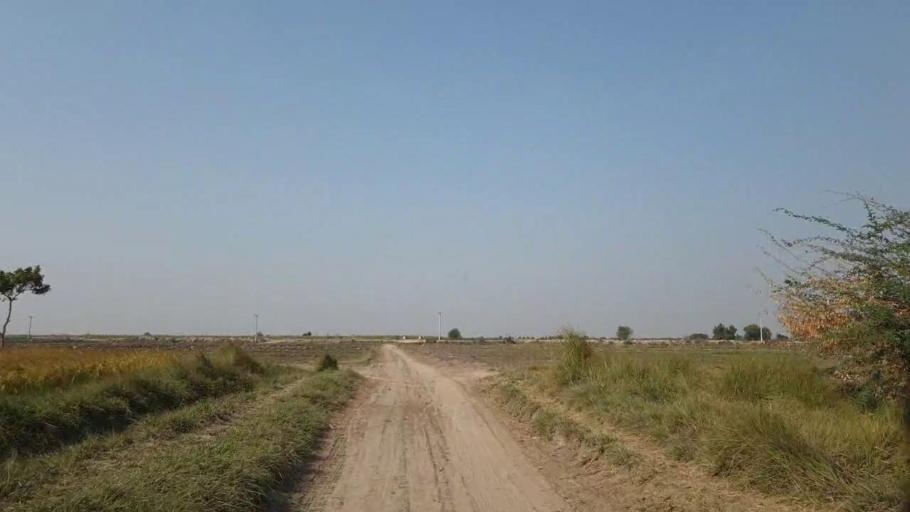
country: PK
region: Sindh
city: Bulri
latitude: 24.9501
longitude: 68.3788
